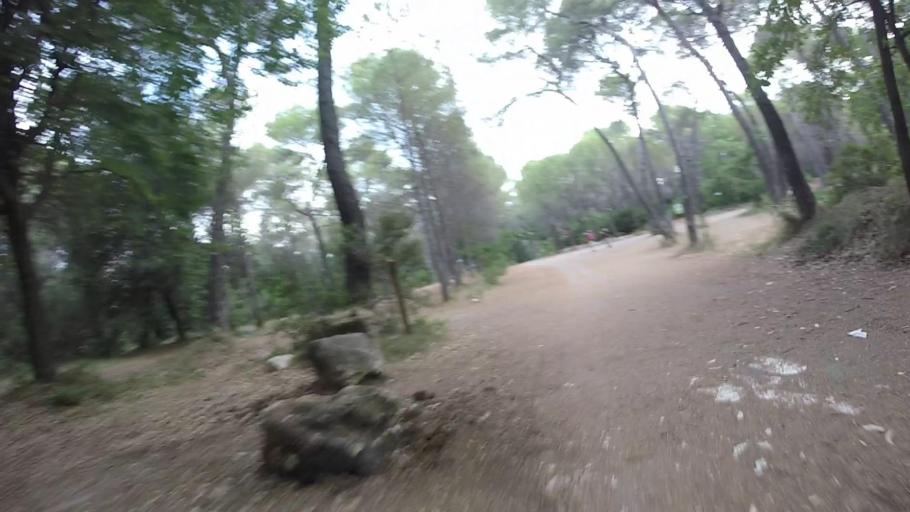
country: FR
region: Provence-Alpes-Cote d'Azur
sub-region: Departement des Alpes-Maritimes
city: Vallauris
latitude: 43.6088
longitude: 7.0416
